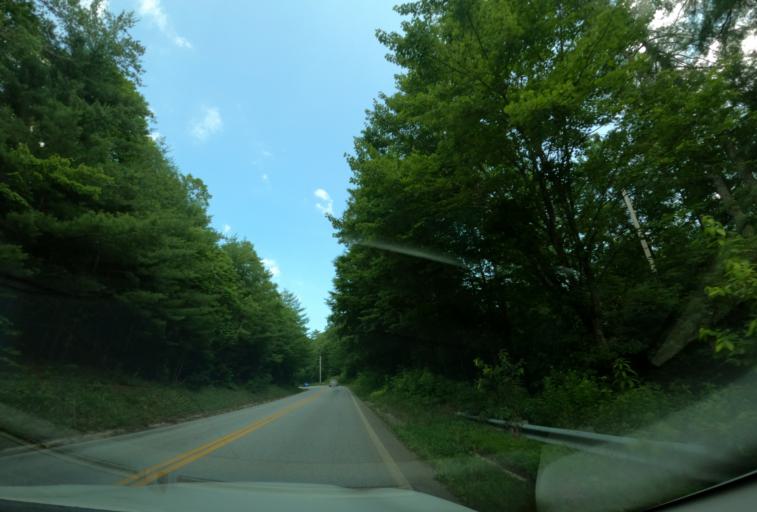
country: US
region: North Carolina
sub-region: Transylvania County
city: Brevard
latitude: 35.1004
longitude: -82.9655
